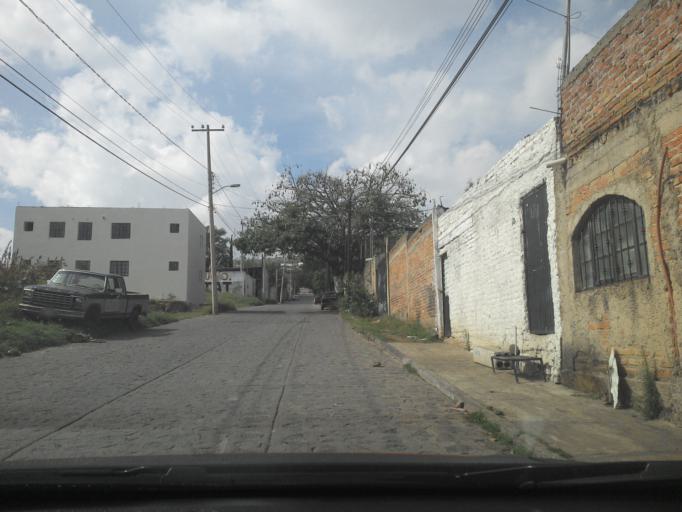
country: MX
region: Jalisco
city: Las Pintas de Arriba
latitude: 20.5942
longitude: -103.3487
